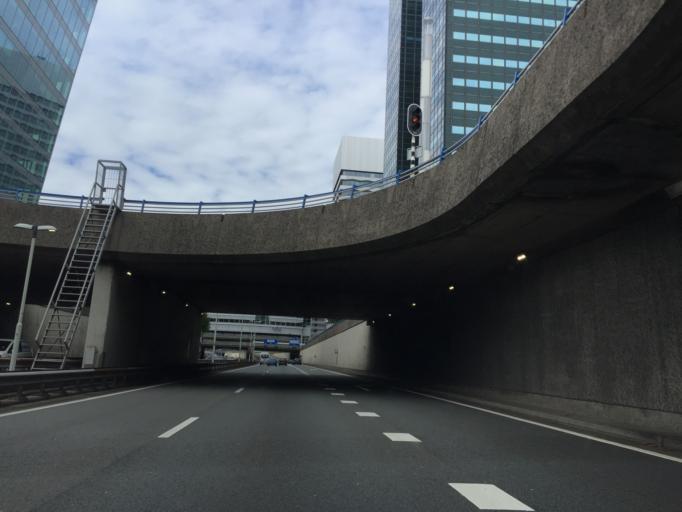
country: NL
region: South Holland
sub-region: Gemeente Leidschendam-Voorburg
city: Voorburg
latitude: 52.0776
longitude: 4.3357
